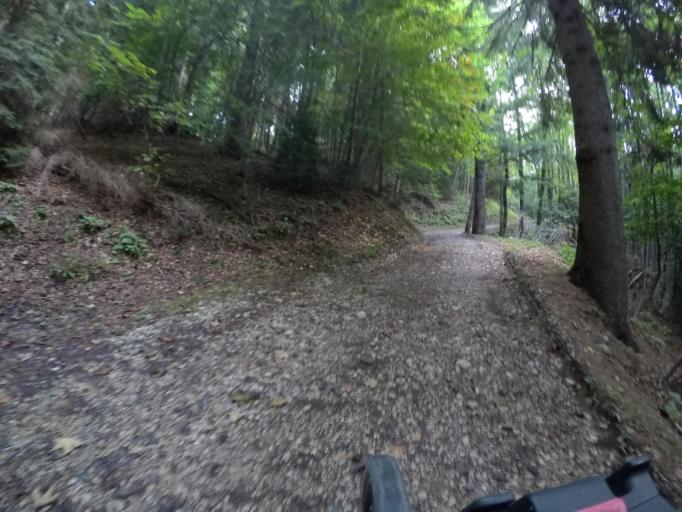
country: IT
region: Friuli Venezia Giulia
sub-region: Provincia di Udine
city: Paularo
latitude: 46.4978
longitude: 13.1885
